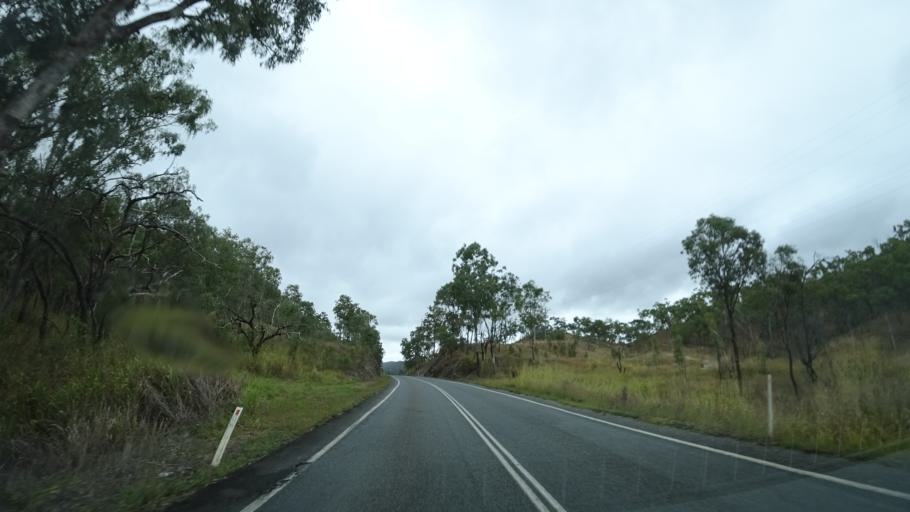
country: AU
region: Queensland
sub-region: Cairns
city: Port Douglas
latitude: -16.7057
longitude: 145.3482
